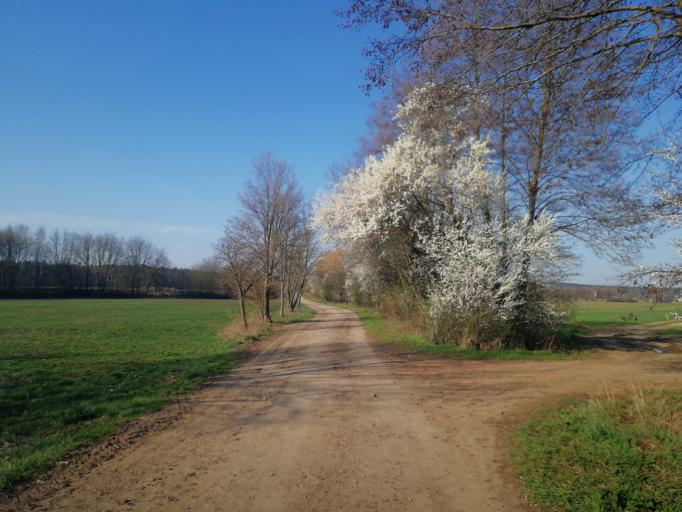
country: DE
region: Brandenburg
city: Luckau
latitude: 51.8391
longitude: 13.6303
